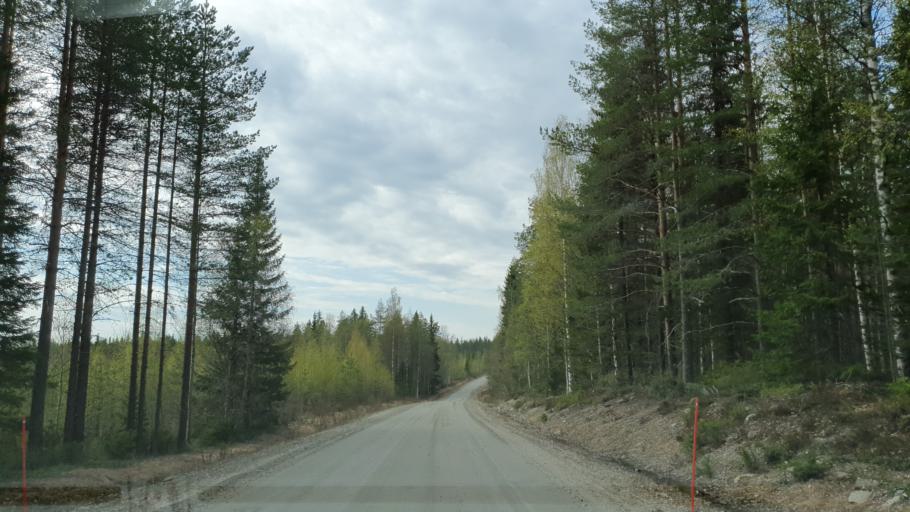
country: FI
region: Kainuu
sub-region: Kehys-Kainuu
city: Kuhmo
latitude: 64.0988
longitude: 29.9355
